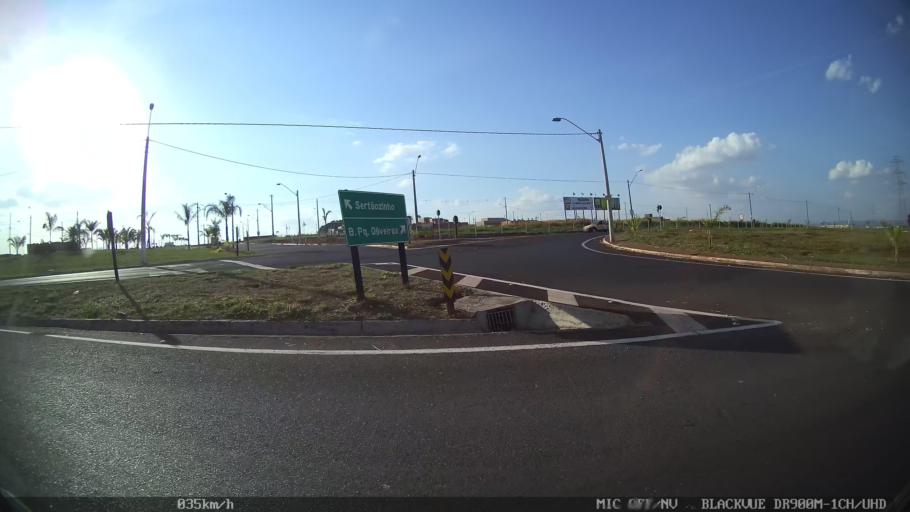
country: BR
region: Sao Paulo
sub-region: Ribeirao Preto
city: Ribeirao Preto
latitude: -21.1261
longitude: -47.8445
